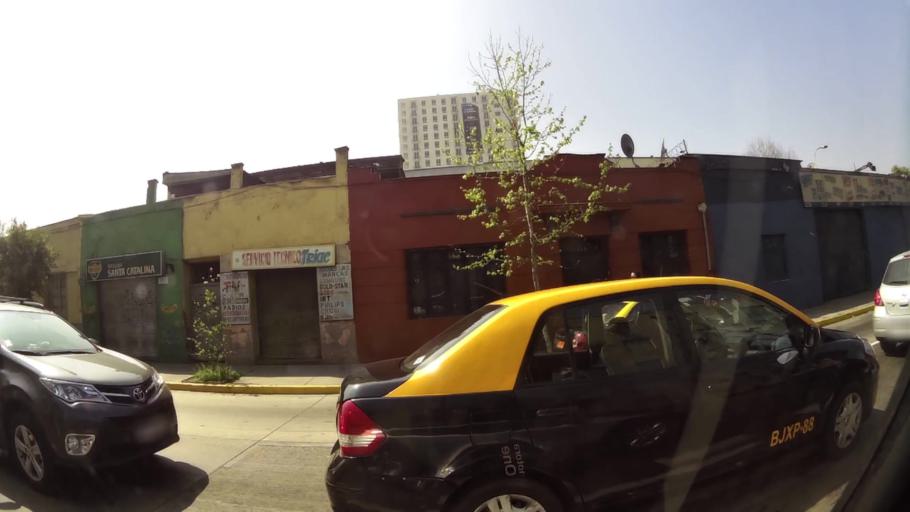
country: CL
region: Santiago Metropolitan
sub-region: Provincia de Santiago
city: Santiago
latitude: -33.4584
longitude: -70.6453
